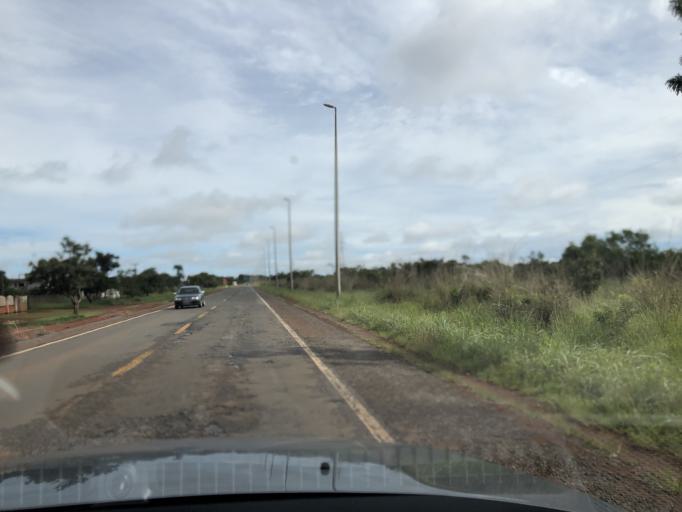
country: BR
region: Federal District
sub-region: Brasilia
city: Brasilia
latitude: -15.6956
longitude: -48.0886
